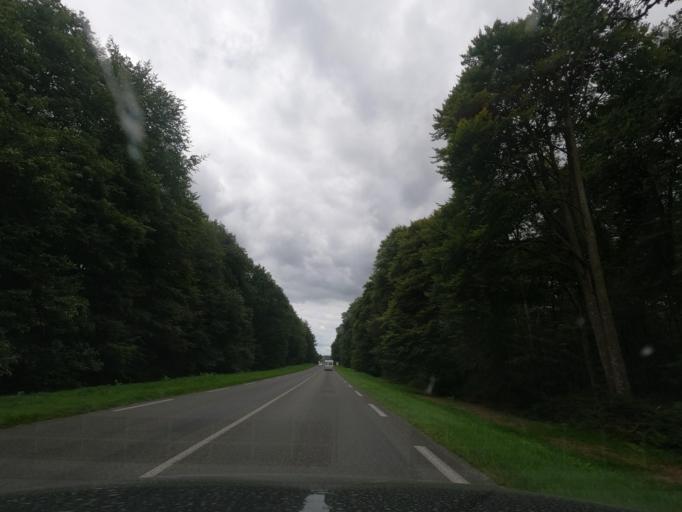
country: FR
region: Brittany
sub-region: Departement d'Ille-et-Vilaine
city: Landean
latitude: 48.4060
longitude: -1.1565
